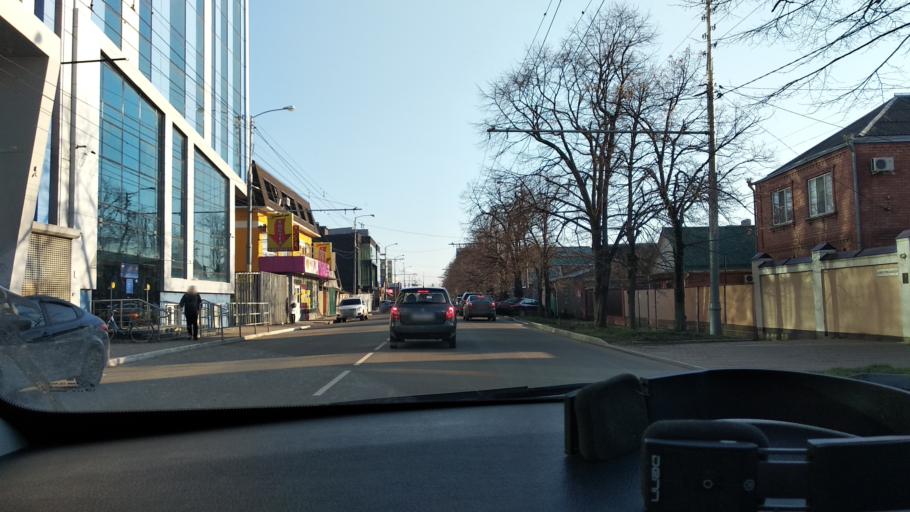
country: RU
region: Adygeya
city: Yablonovskiy
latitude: 45.0037
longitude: 38.9609
